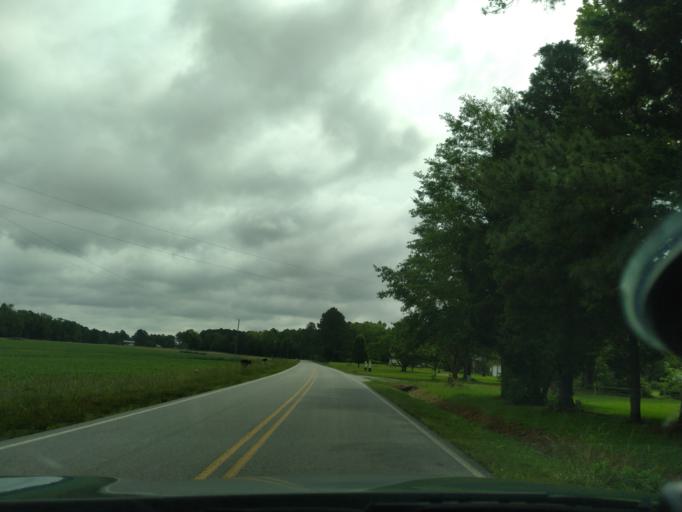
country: US
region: North Carolina
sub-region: Washington County
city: Plymouth
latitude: 35.8569
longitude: -76.7167
